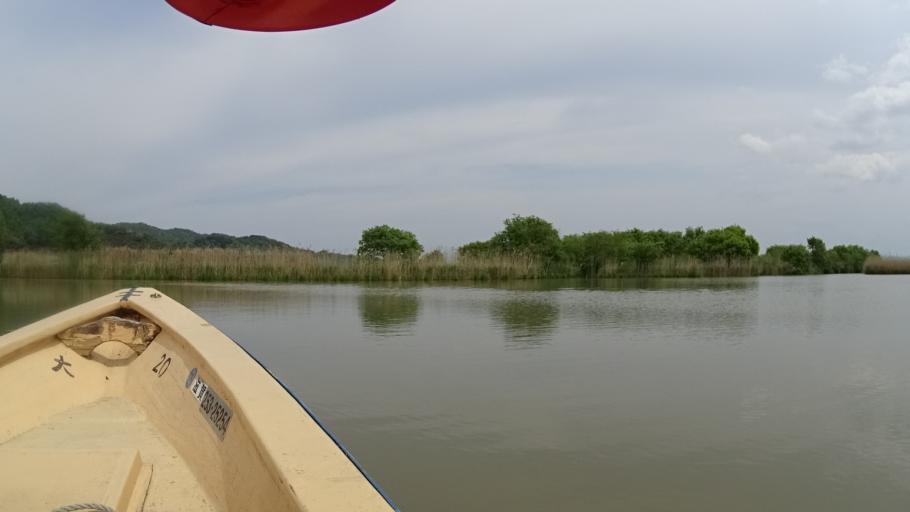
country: JP
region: Shiga Prefecture
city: Omihachiman
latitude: 35.1567
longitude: 136.1011
